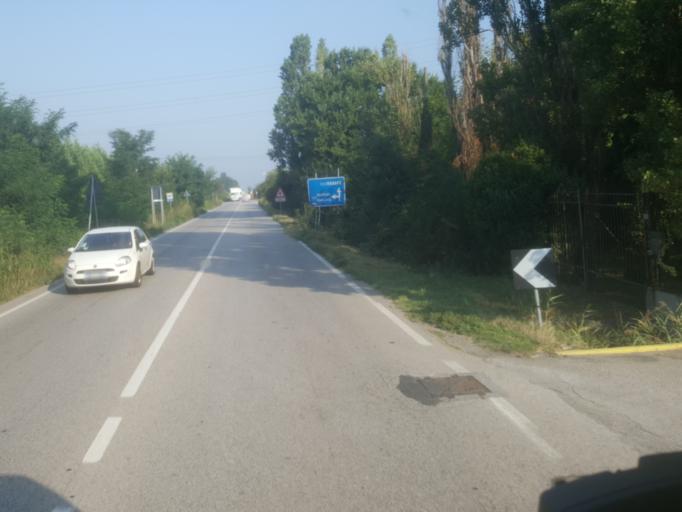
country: IT
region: Emilia-Romagna
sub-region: Provincia di Ravenna
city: Fornace Zarattini
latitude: 44.4302
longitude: 12.1519
